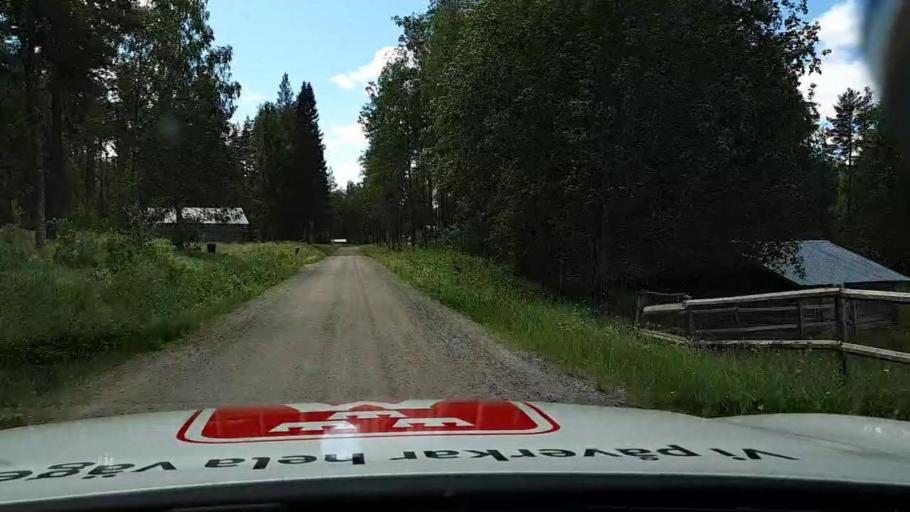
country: SE
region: Jaemtland
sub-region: Braecke Kommun
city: Braecke
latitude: 62.7545
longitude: 15.5034
